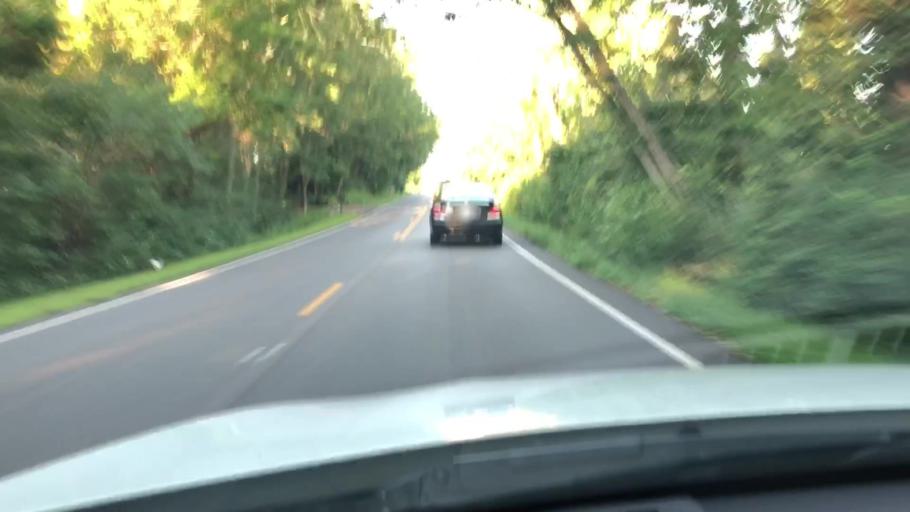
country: US
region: Kentucky
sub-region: Jefferson County
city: Middletown
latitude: 38.2192
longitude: -85.5193
